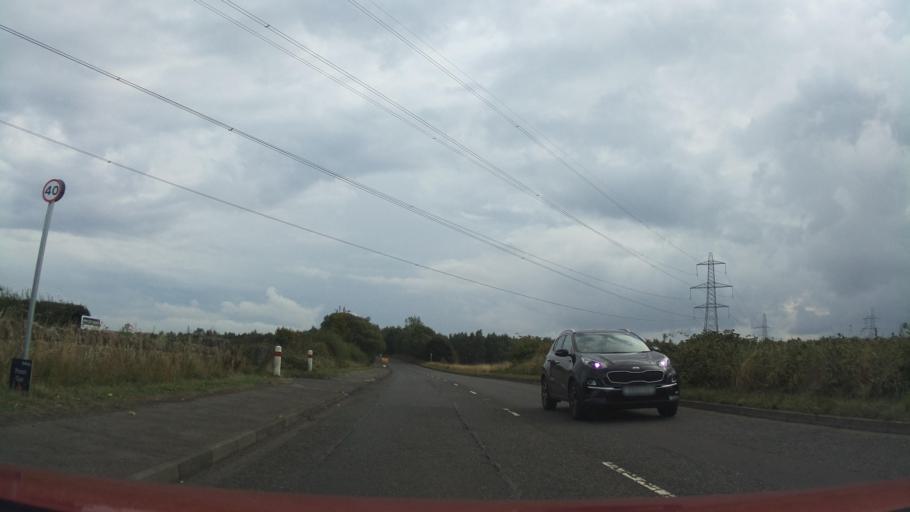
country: GB
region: Scotland
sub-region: East Lothian
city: Cockenzie
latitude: 55.9608
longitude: -2.9564
